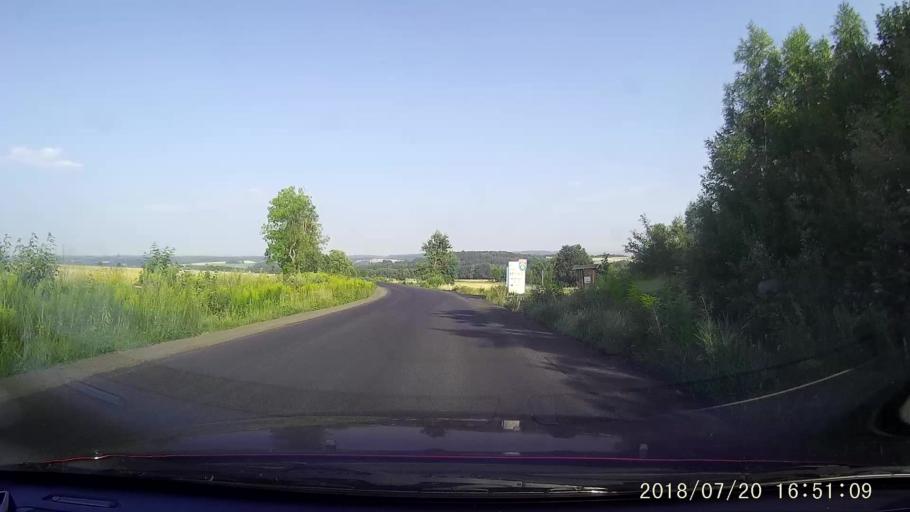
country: PL
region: Lower Silesian Voivodeship
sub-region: Powiat lubanski
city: Lesna
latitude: 51.0390
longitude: 15.2163
